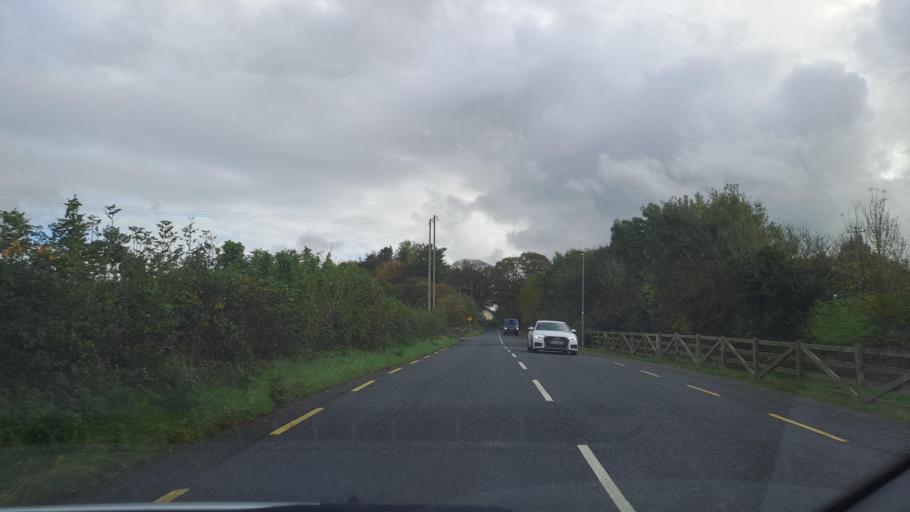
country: IE
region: Ulster
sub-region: An Cabhan
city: Virginia
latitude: 53.8299
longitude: -7.0603
